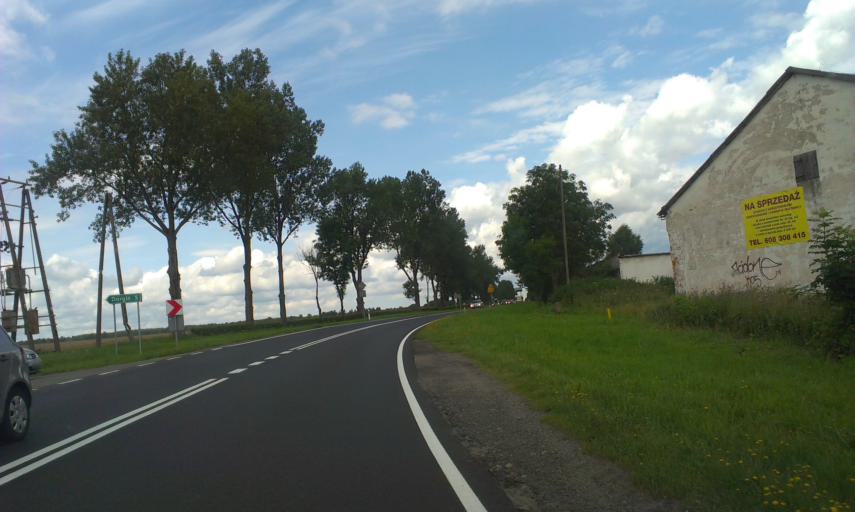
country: PL
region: West Pomeranian Voivodeship
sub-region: Powiat koszalinski
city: Bobolice
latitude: 54.0446
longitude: 16.4415
